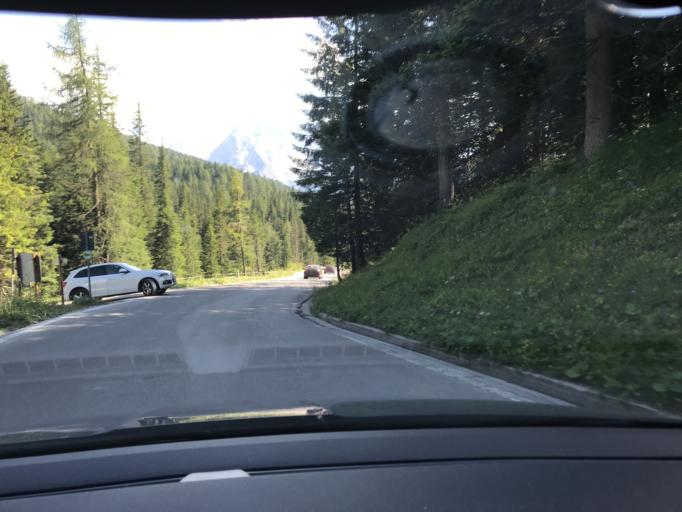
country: IT
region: Veneto
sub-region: Provincia di Belluno
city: Cortina d'Ampezzo
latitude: 46.5915
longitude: 12.2628
